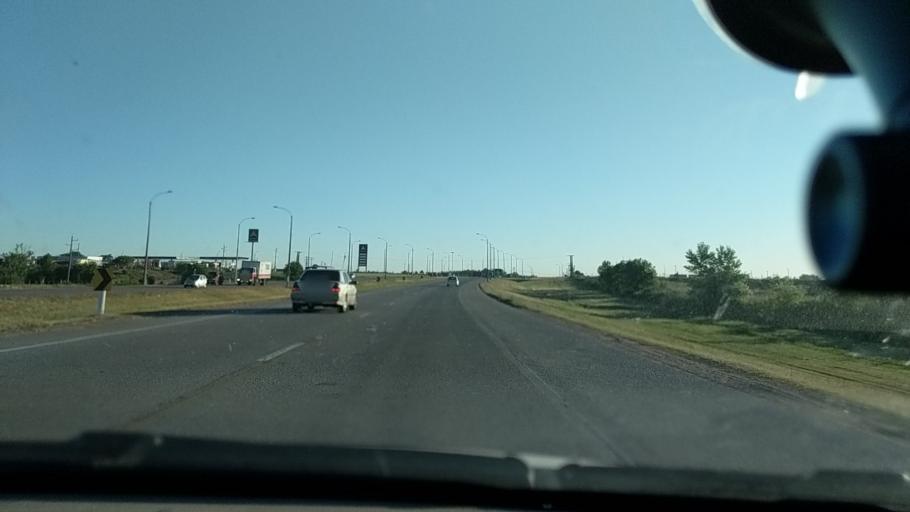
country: UY
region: Canelones
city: La Paz
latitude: -34.7462
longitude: -56.2533
